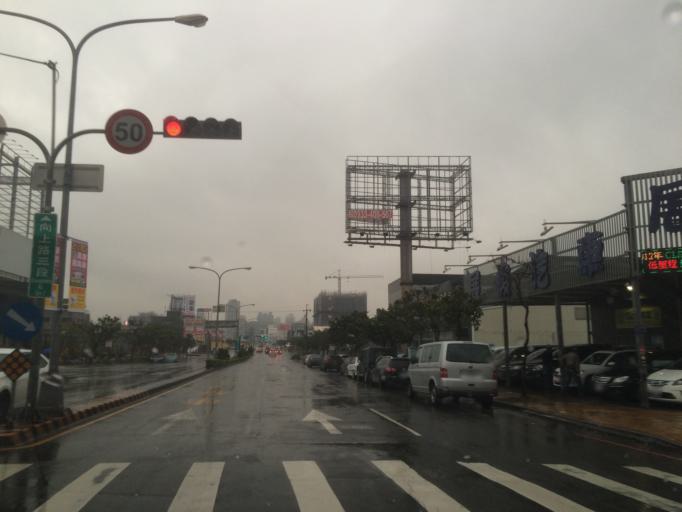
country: TW
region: Taiwan
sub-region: Taichung City
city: Taichung
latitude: 24.1451
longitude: 120.6234
